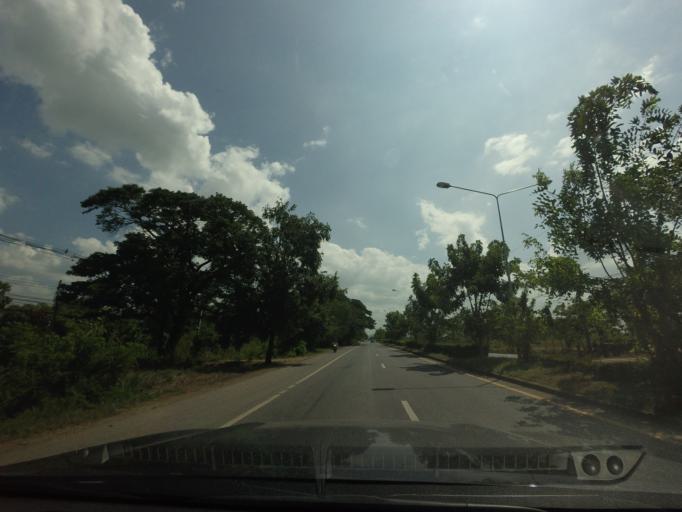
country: TH
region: Phetchabun
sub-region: Amphoe Bueng Sam Phan
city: Bueng Sam Phan
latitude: 15.8513
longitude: 101.0110
